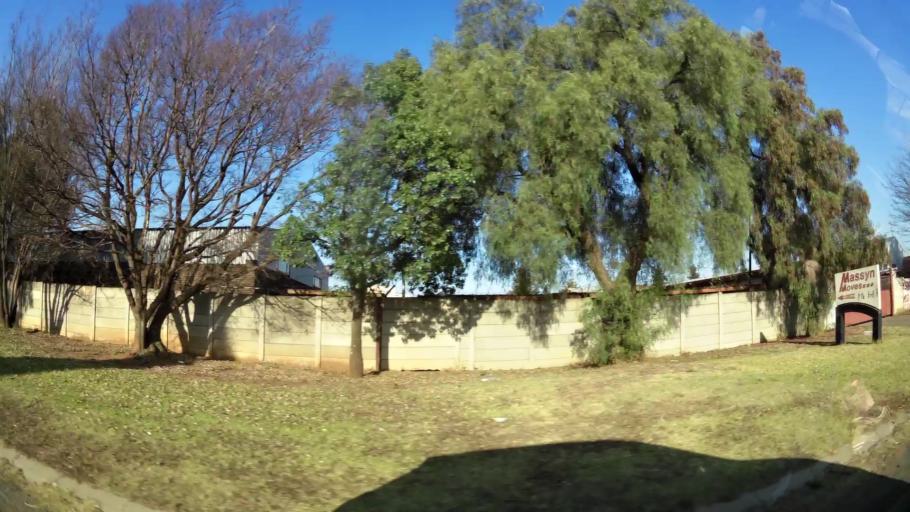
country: ZA
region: Gauteng
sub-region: West Rand District Municipality
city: Randfontein
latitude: -26.2056
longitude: 27.6942
